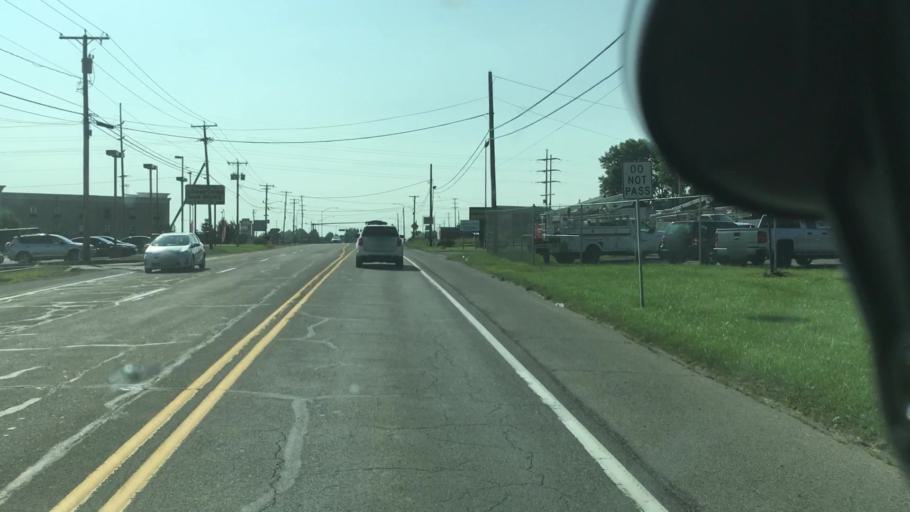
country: US
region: Pennsylvania
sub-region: Lawrence County
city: Oakwood
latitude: 41.0144
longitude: -80.4010
